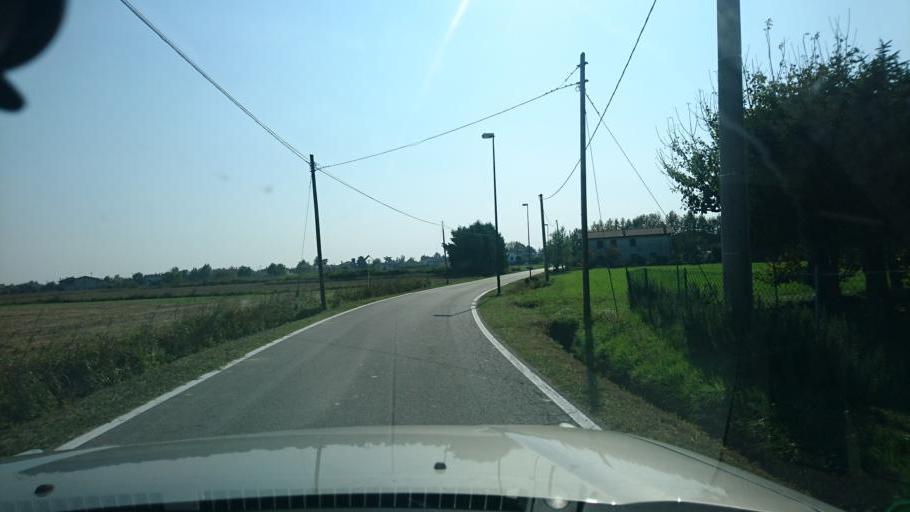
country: IT
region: Veneto
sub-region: Provincia di Vicenza
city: Camisano Vicentino
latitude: 45.5259
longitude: 11.7291
